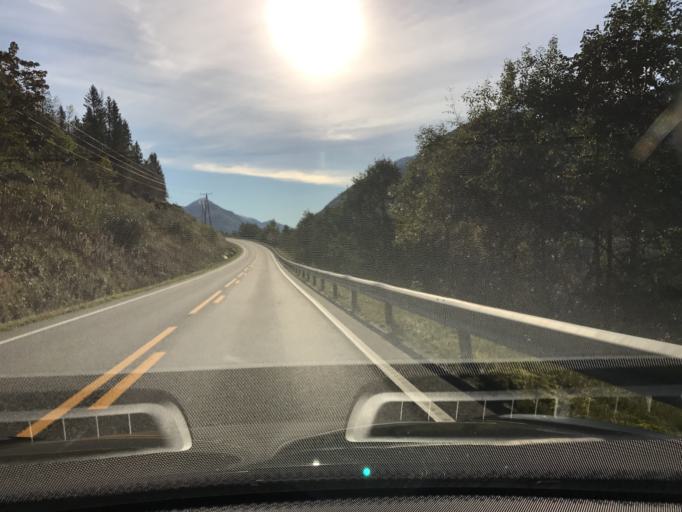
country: NO
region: Sogn og Fjordane
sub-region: Leikanger
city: Hermansverk
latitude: 61.4132
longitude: 6.7613
